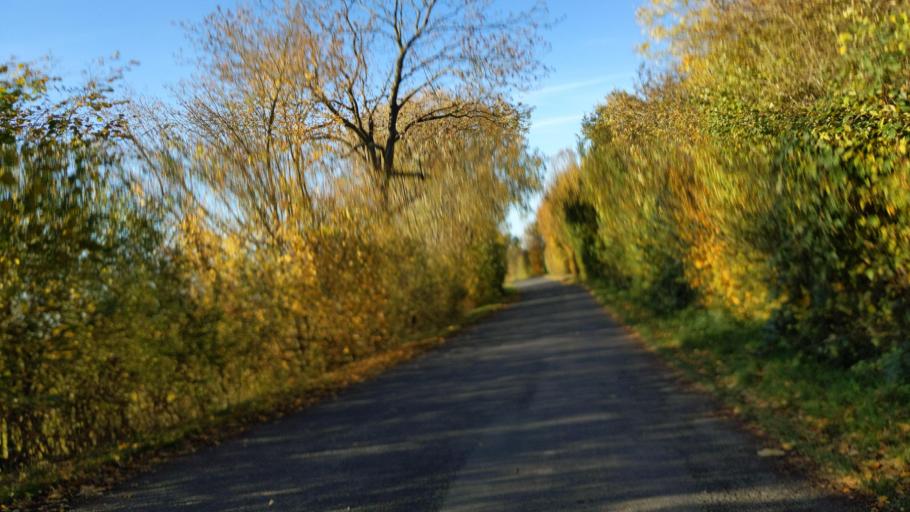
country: DE
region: Schleswig-Holstein
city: Gross Disnack
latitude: 53.7394
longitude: 10.7046
